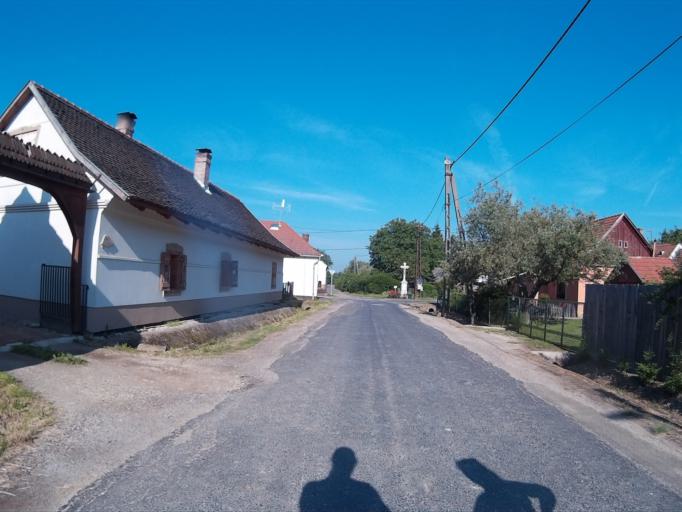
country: AT
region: Burgenland
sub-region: Politischer Bezirk Gussing
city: Heiligenbrunn
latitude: 46.9348
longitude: 16.4814
